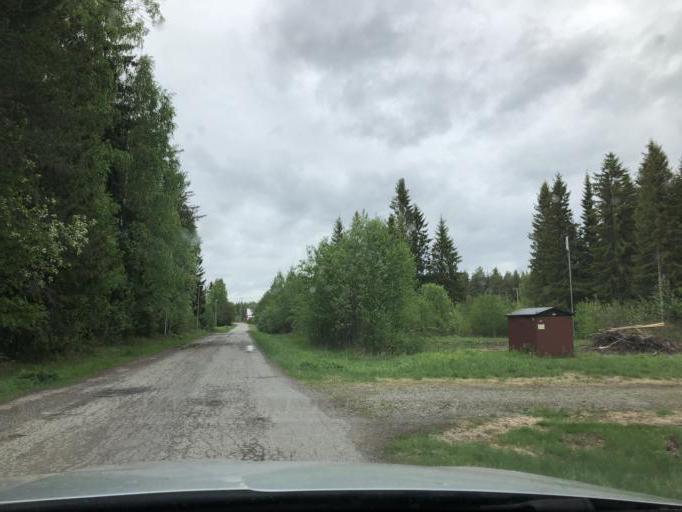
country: SE
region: Norrbotten
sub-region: Pitea Kommun
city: Roknas
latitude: 65.3759
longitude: 21.2796
